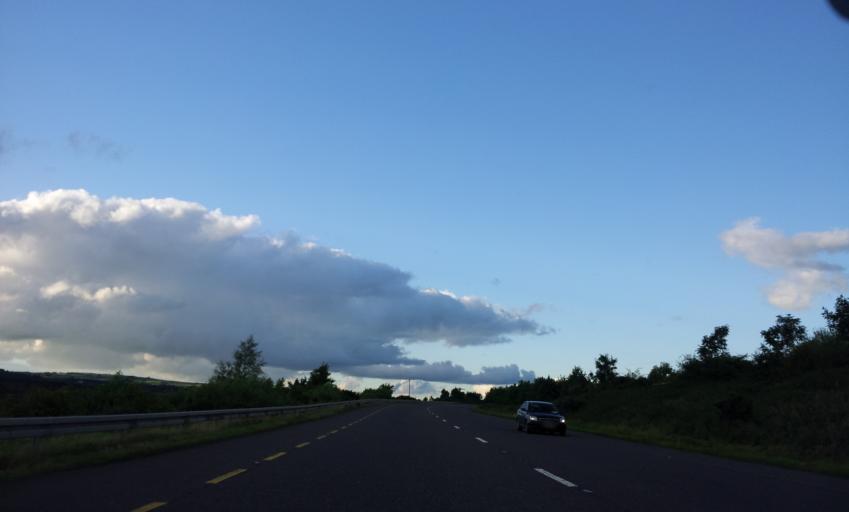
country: IE
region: Munster
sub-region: County Limerick
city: Abbeyfeale
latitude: 52.3274
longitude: -9.3592
